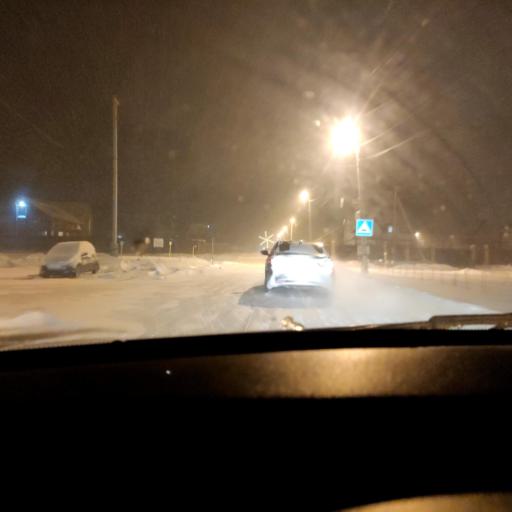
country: RU
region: Perm
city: Kultayevo
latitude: 57.8579
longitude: 55.9224
